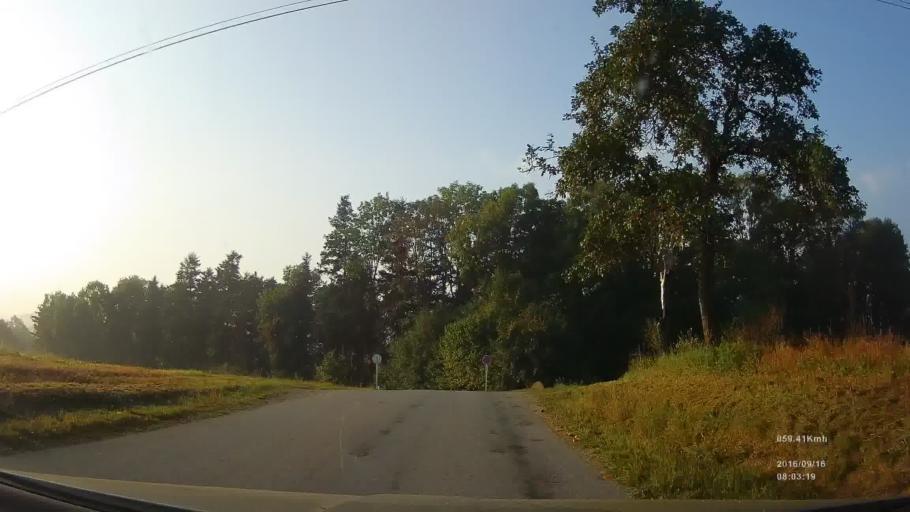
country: SK
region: Presovsky
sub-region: Okres Presov
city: Presov
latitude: 48.9042
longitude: 21.1867
